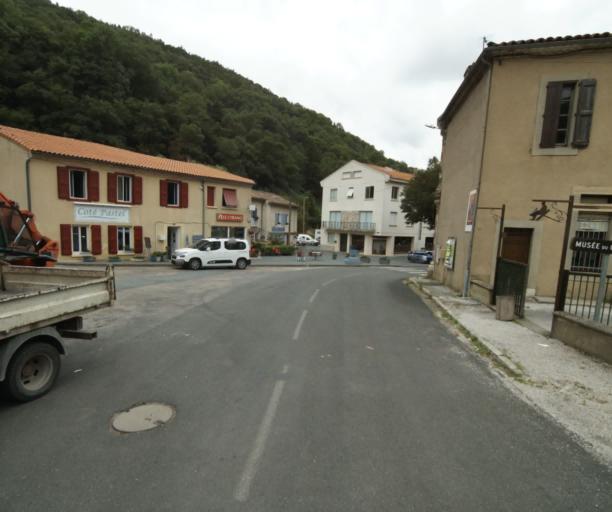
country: FR
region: Midi-Pyrenees
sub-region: Departement du Tarn
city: Soreze
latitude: 43.4385
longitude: 2.0670
